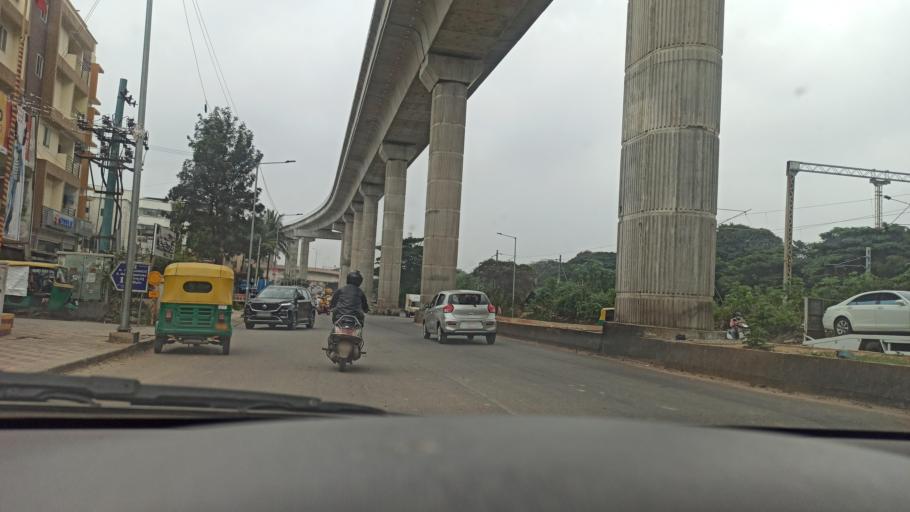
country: IN
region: Karnataka
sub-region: Bangalore Urban
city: Bangalore
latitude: 13.0002
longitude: 77.6838
